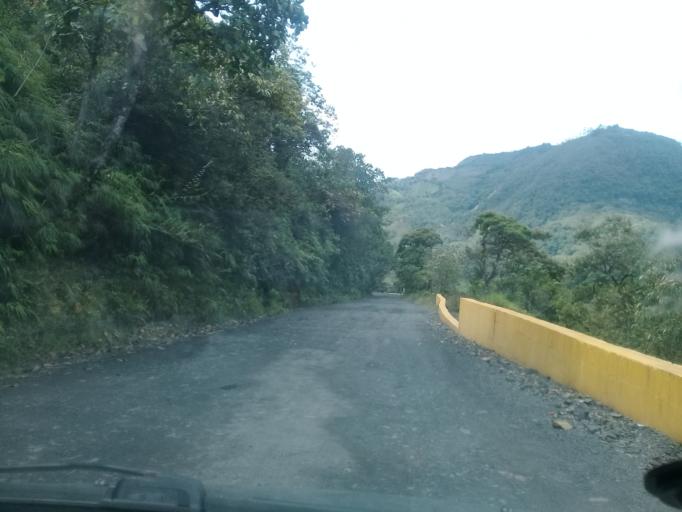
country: CO
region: Cundinamarca
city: Gachala
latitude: 4.7015
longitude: -73.4689
